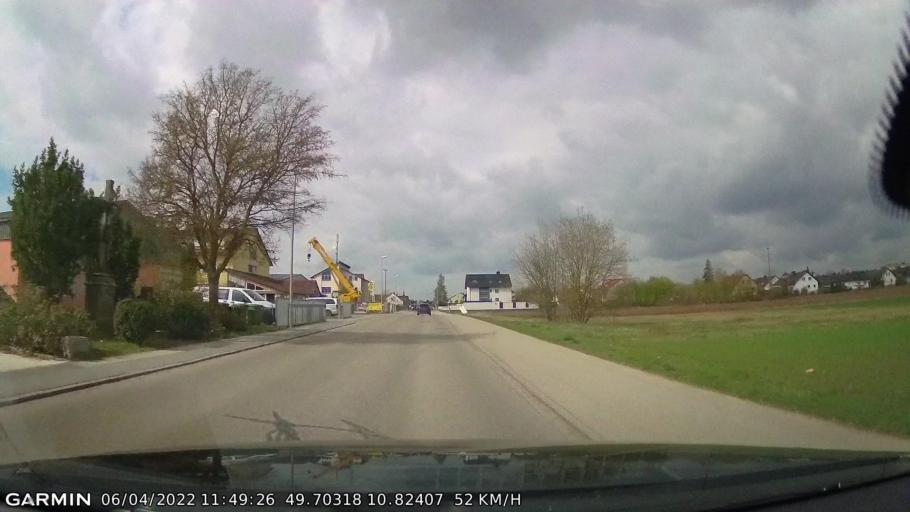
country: DE
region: Bavaria
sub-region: Regierungsbezirk Mittelfranken
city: Hochstadt an der Aisch
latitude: 49.7032
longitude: 10.8241
